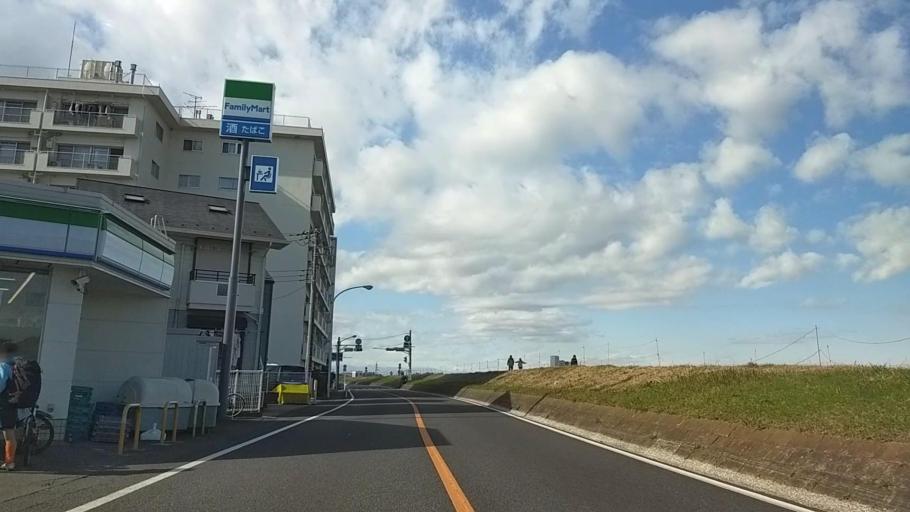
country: JP
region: Kanagawa
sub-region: Kawasaki-shi
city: Kawasaki
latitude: 35.5869
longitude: 139.6617
